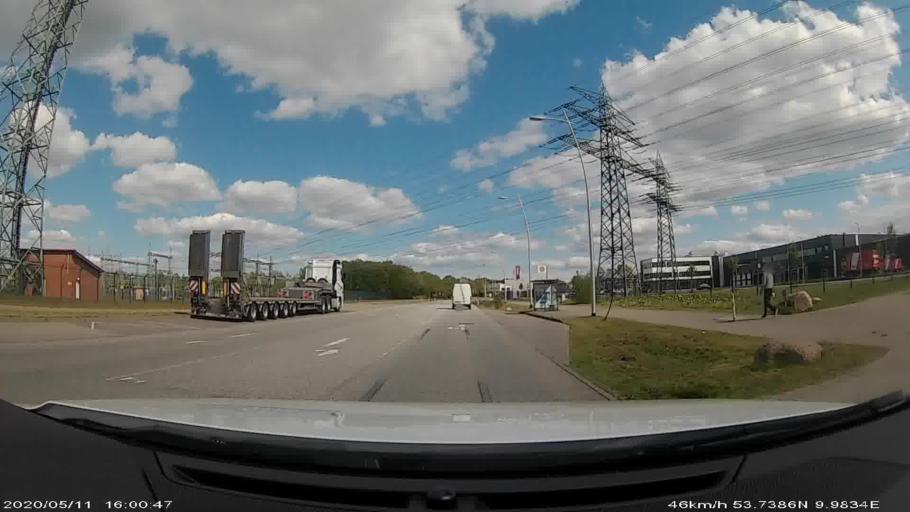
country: DE
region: Schleswig-Holstein
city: Norderstedt
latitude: 53.7345
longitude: 9.9880
